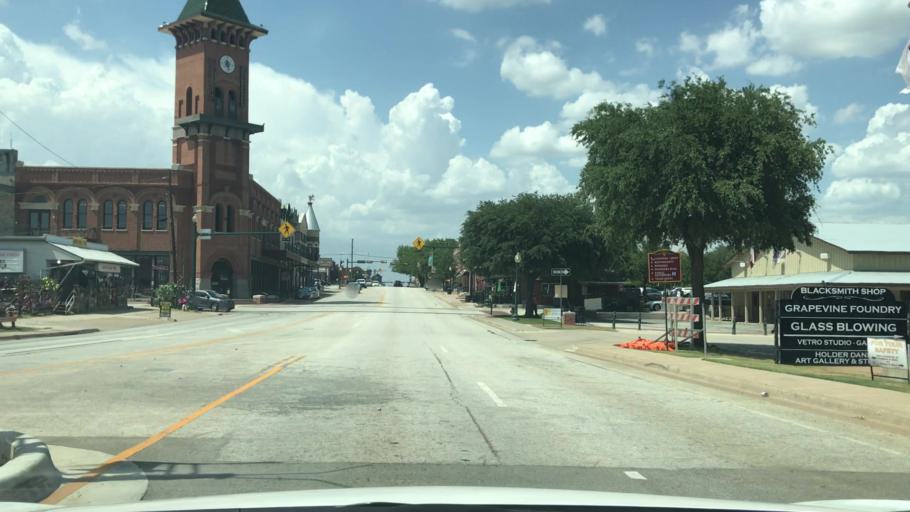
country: US
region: Texas
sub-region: Tarrant County
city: Grapevine
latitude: 32.9337
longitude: -97.0784
